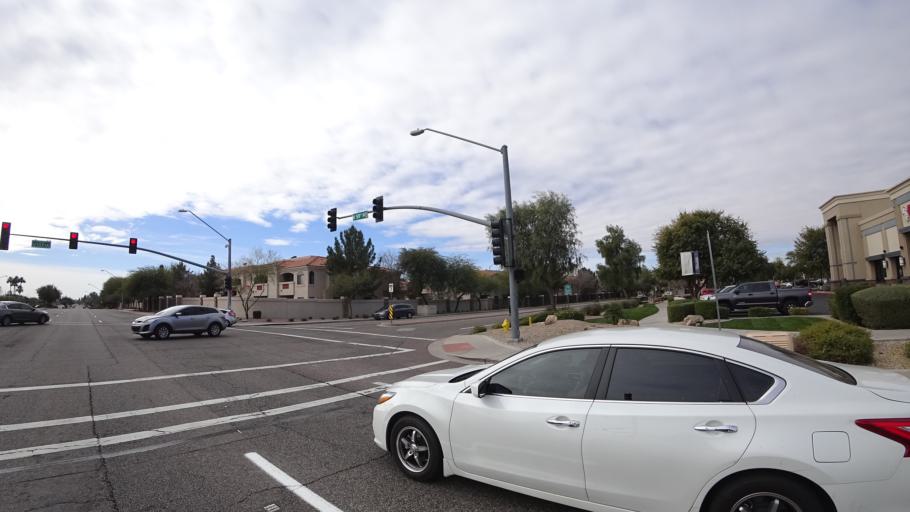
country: US
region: Arizona
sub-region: Maricopa County
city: Peoria
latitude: 33.6616
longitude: -112.1866
